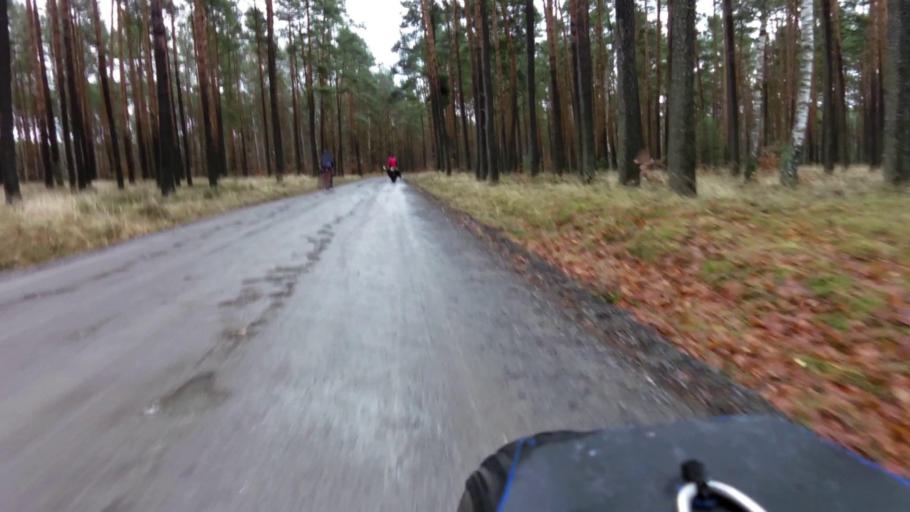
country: PL
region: Lubusz
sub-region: Powiat gorzowski
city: Witnica
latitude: 52.7051
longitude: 14.8286
